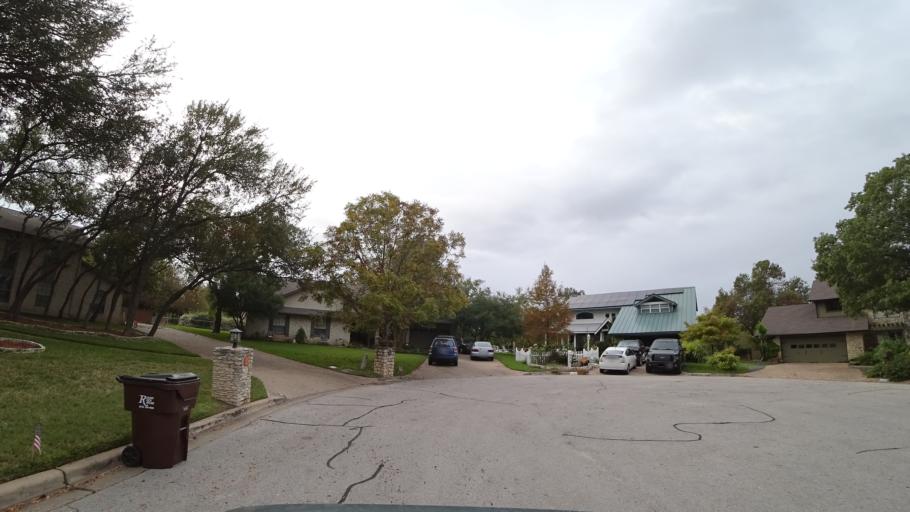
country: US
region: Texas
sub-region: Williamson County
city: Round Rock
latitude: 30.5010
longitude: -97.6926
